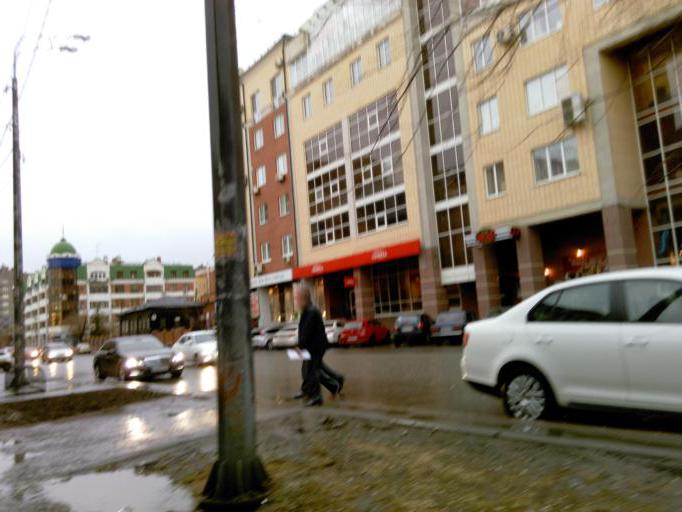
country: RU
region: Tjumen
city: Tyumen
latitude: 57.1566
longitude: 65.5443
